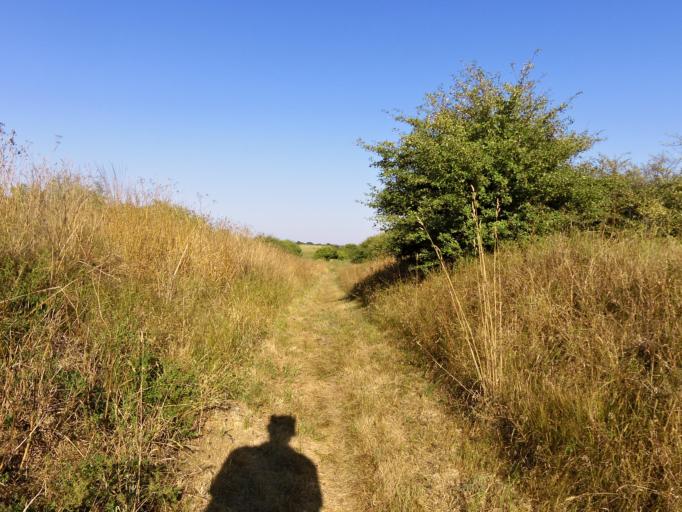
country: DK
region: South Denmark
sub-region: Aabenraa Kommune
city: Rodekro
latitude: 55.1019
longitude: 9.3455
